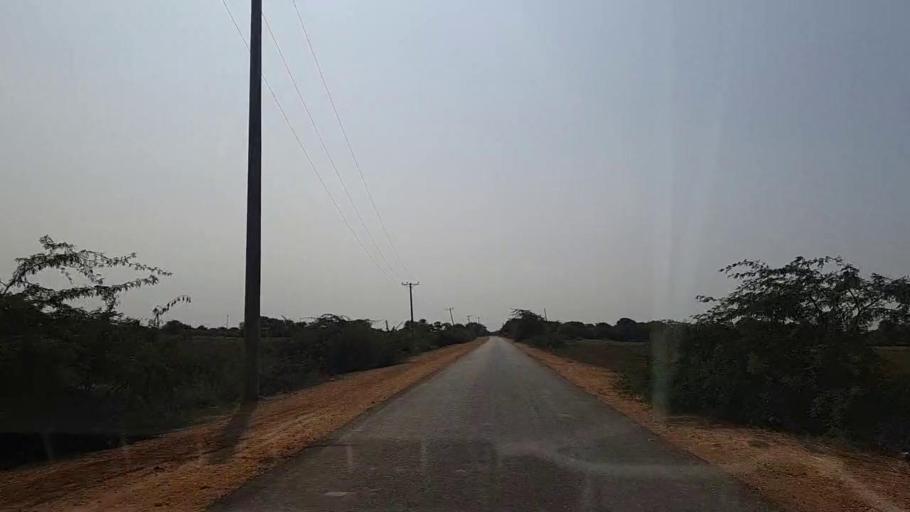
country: PK
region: Sindh
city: Chuhar Jamali
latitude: 24.3263
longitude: 67.9429
